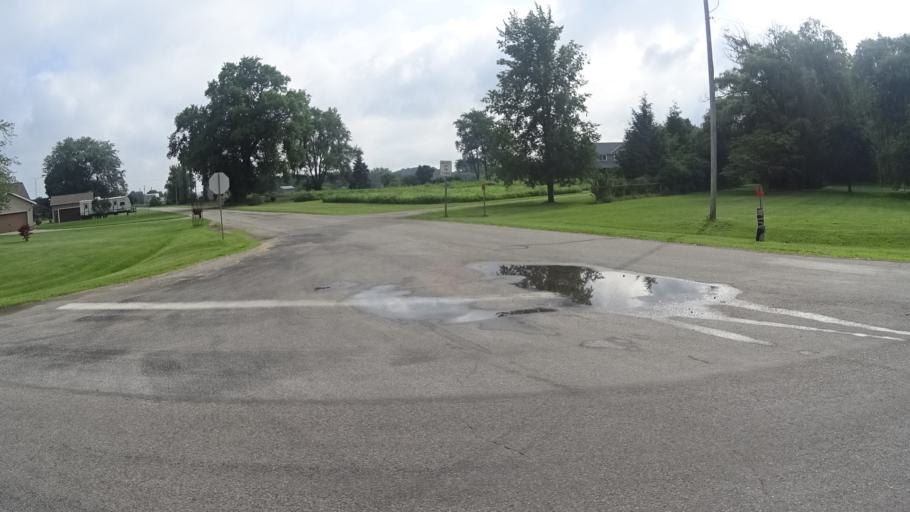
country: US
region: Ohio
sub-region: Erie County
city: Huron
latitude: 41.3512
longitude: -82.5158
